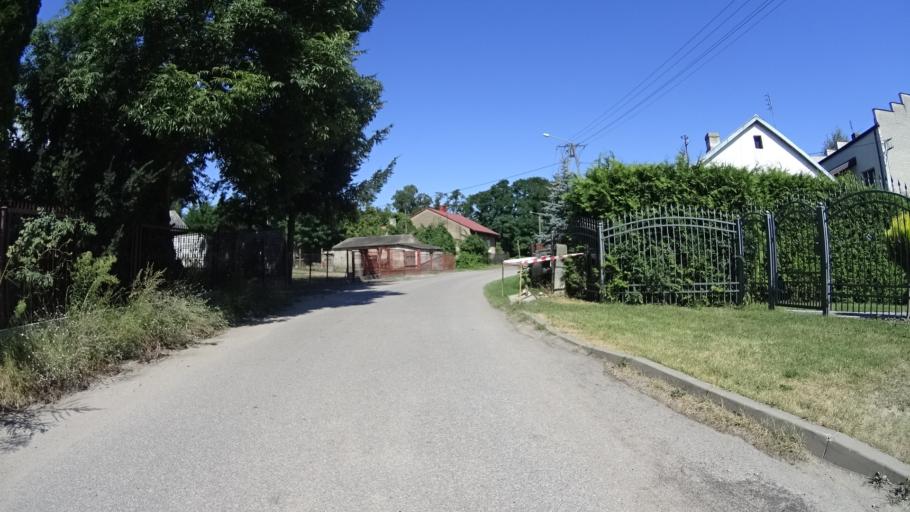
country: PL
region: Masovian Voivodeship
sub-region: Powiat bialobrzeski
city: Promna
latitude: 51.6723
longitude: 20.9422
